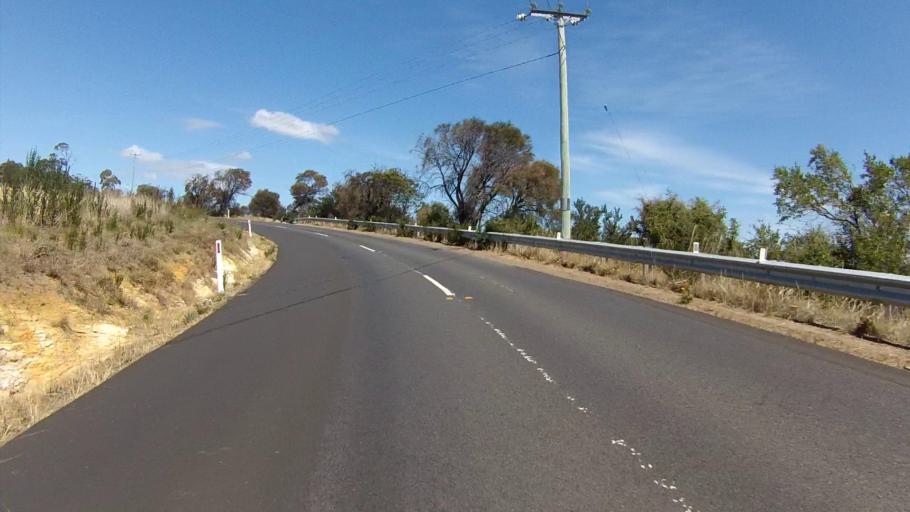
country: AU
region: Tasmania
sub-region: Sorell
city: Sorell
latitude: -42.7878
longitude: 147.5200
